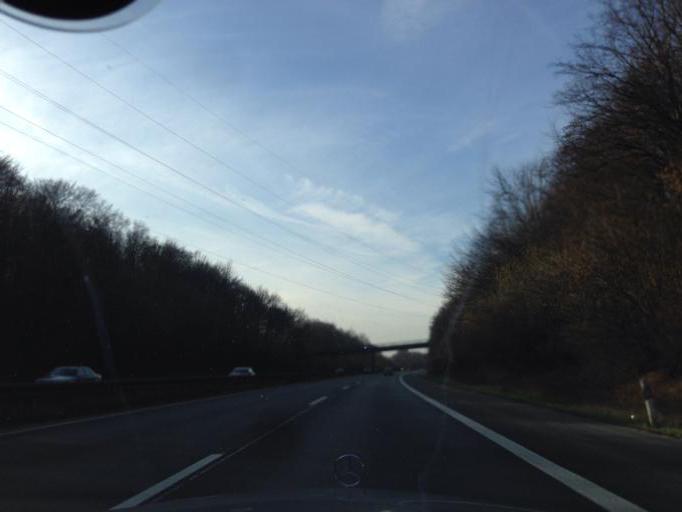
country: DE
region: North Rhine-Westphalia
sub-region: Regierungsbezirk Munster
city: Tecklenburg
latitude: 52.2524
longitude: 7.8060
